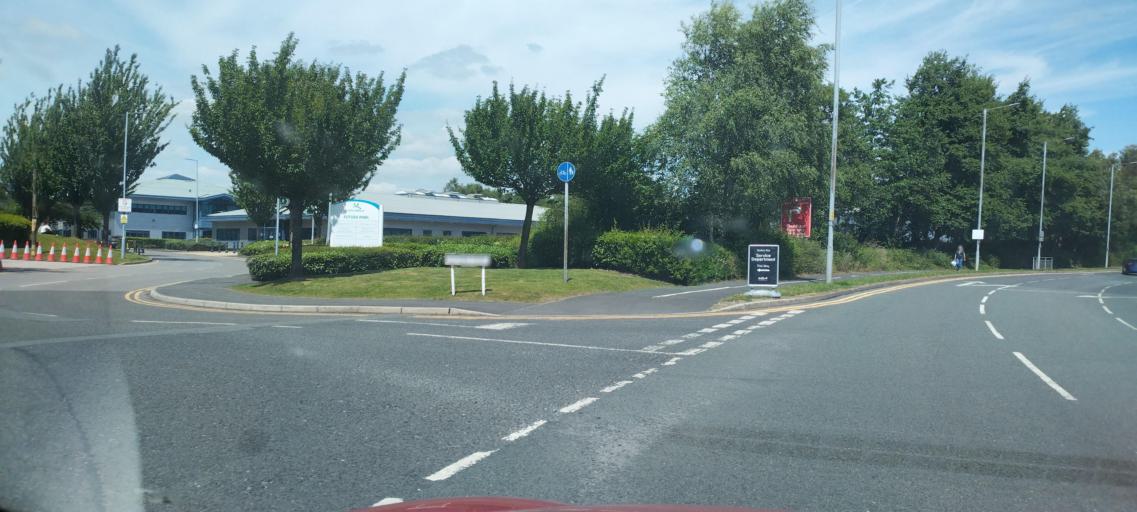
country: GB
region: England
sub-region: Borough of Bolton
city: Horwich
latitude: 53.5847
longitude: -2.5416
